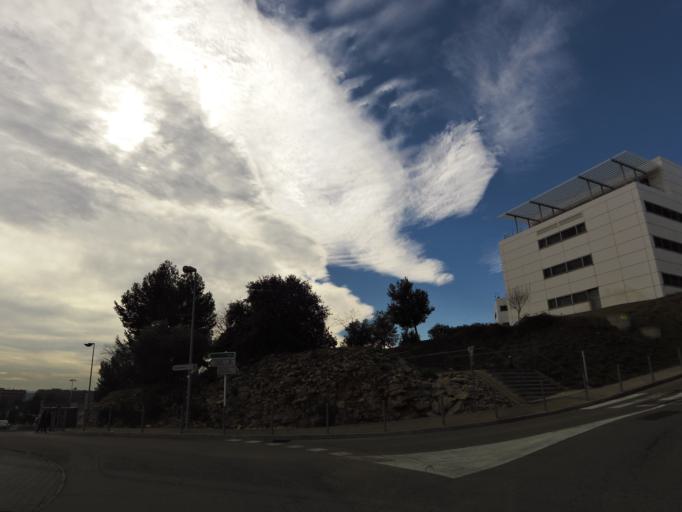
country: FR
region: Languedoc-Roussillon
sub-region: Departement du Gard
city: Nimes
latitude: 43.8235
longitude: 4.3191
